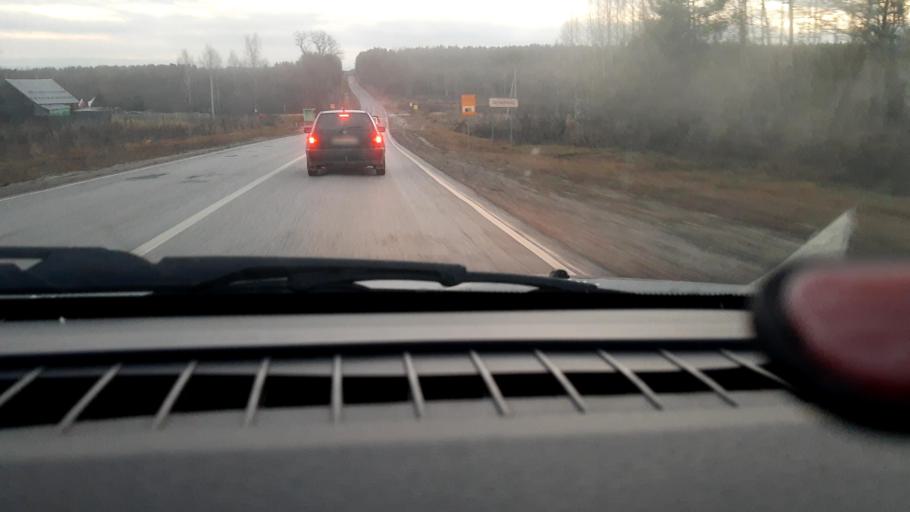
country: RU
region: Nizjnij Novgorod
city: Krasnyye Baki
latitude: 57.0451
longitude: 45.1327
